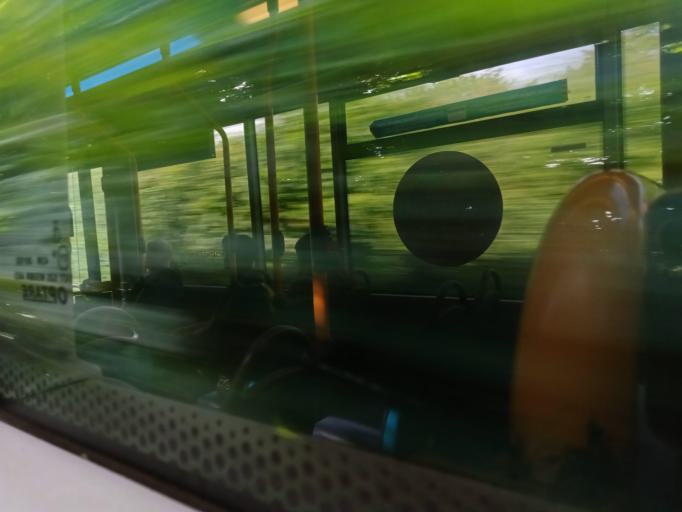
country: GB
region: Wales
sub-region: Anglesey
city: Llangoed
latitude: 53.3012
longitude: -4.0844
